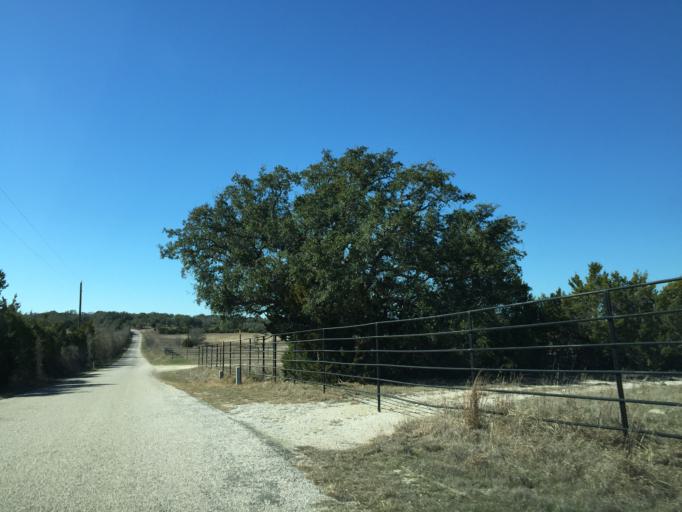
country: US
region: Texas
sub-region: Lampasas County
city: Kempner
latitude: 30.9319
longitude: -98.0370
